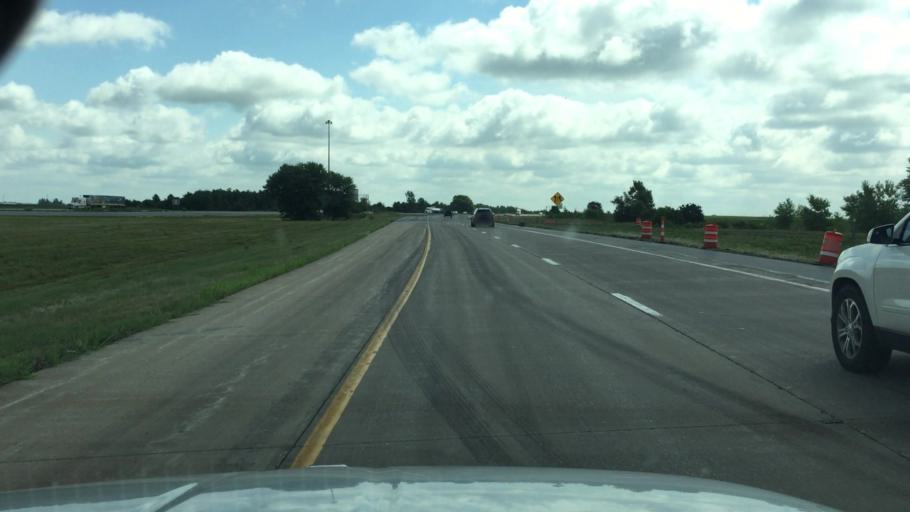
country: US
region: Iowa
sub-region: Scott County
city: Walcott
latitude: 41.6029
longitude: -90.6729
